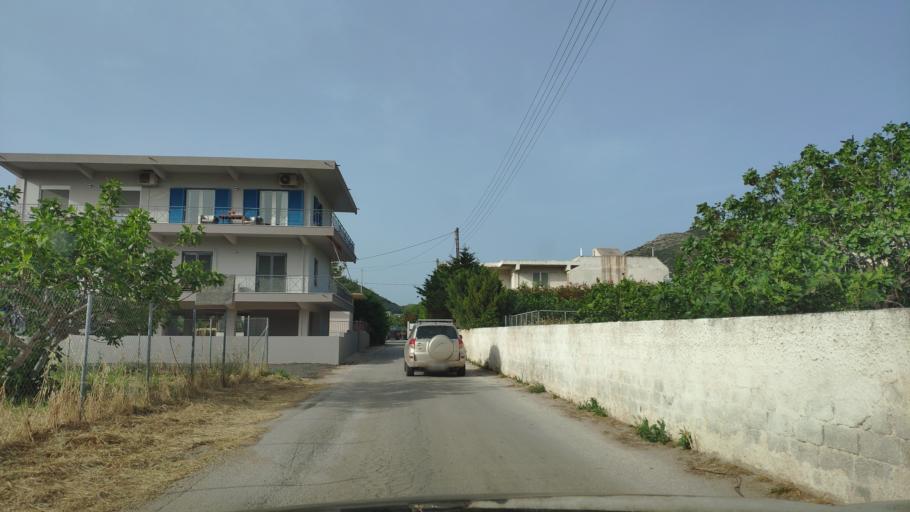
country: GR
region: Attica
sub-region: Nomarchia Anatolikis Attikis
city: Limin Mesoyaias
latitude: 37.8679
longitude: 24.0288
